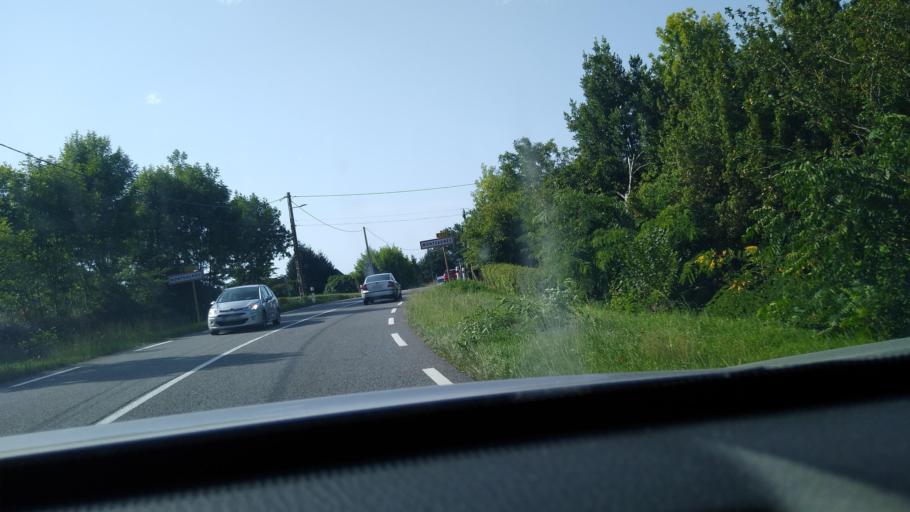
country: FR
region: Midi-Pyrenees
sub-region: Departement de la Haute-Garonne
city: Salies-du-Salat
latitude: 43.1053
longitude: 0.9403
